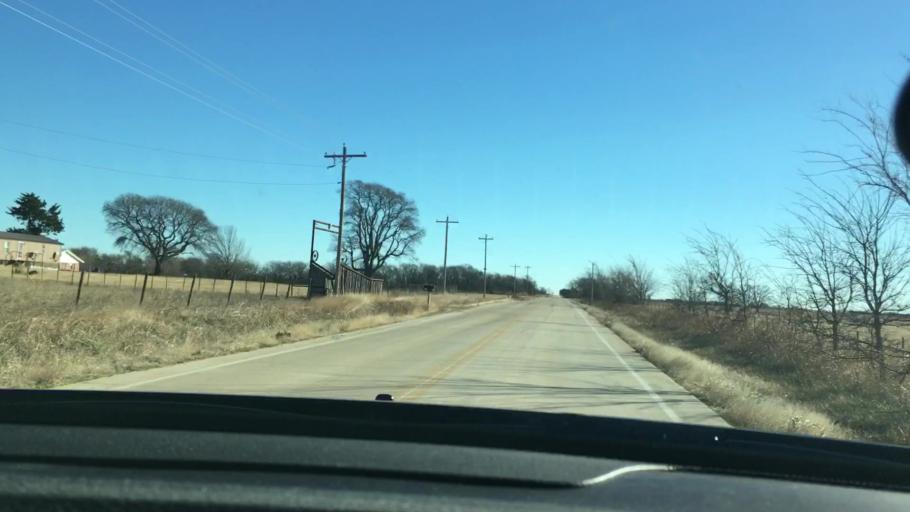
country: US
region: Oklahoma
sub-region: Marshall County
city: Madill
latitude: 34.1144
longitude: -96.6833
